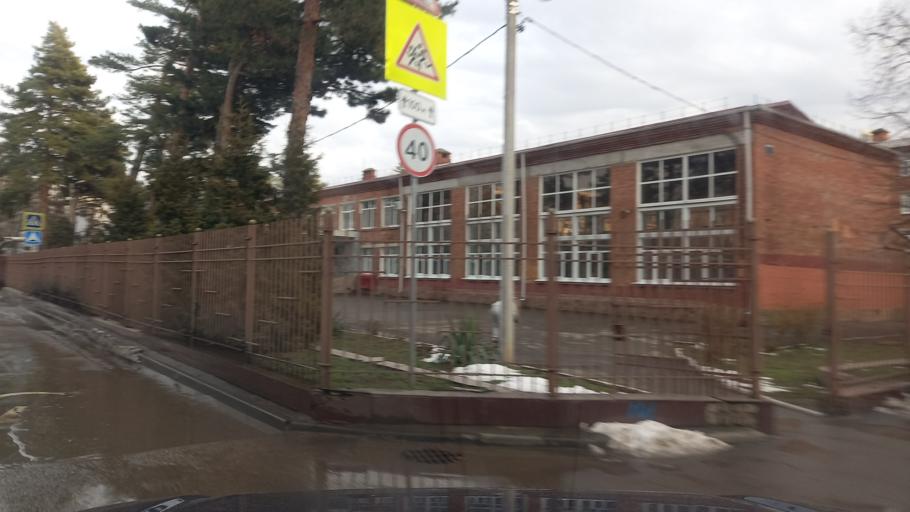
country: RU
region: Krasnodarskiy
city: Pashkovskiy
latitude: 45.0195
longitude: 39.0461
